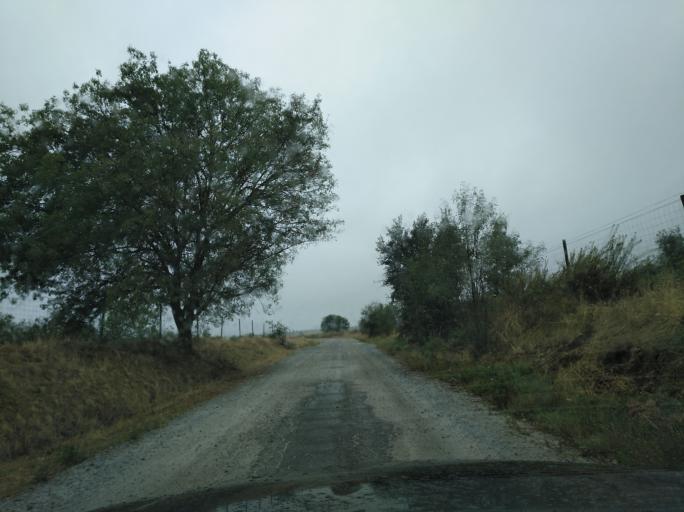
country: PT
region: Portalegre
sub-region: Campo Maior
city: Campo Maior
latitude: 38.9754
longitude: -7.0799
